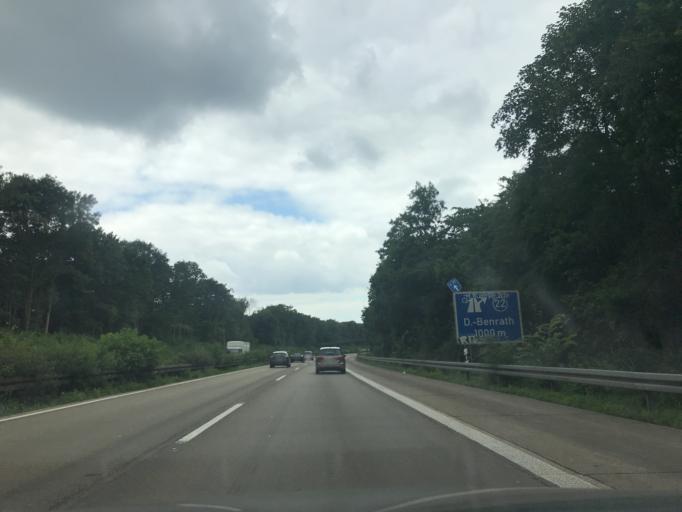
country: DE
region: North Rhine-Westphalia
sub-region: Regierungsbezirk Dusseldorf
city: Hilden
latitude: 51.1666
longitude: 6.8877
